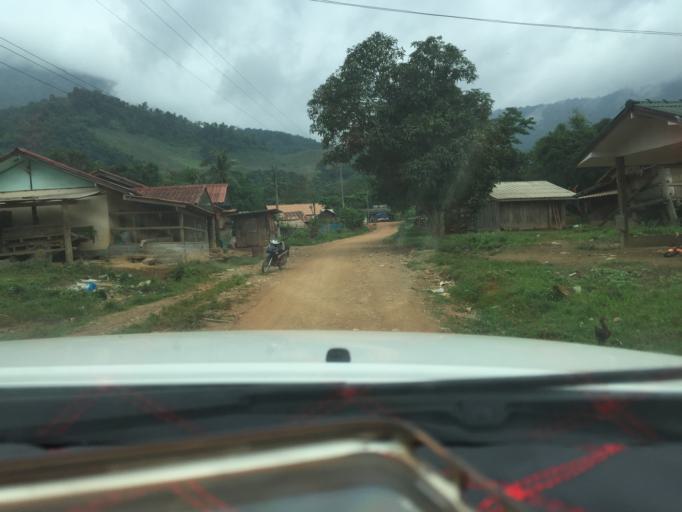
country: TH
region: Phayao
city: Phu Sang
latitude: 19.7436
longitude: 100.4321
